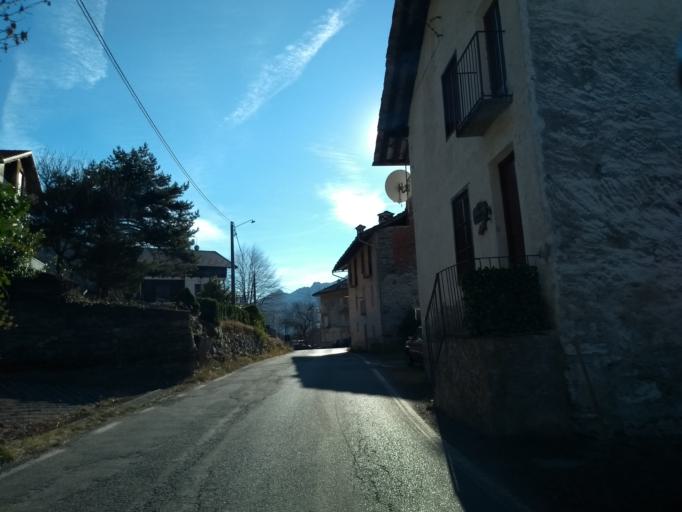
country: IT
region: Piedmont
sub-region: Provincia di Torino
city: Cantoira
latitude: 45.3293
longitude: 7.3948
